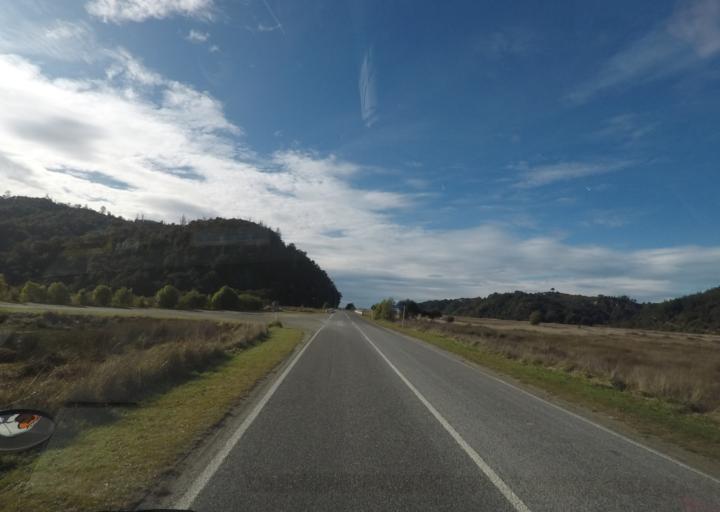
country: NZ
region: Tasman
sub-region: Tasman District
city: Motueka
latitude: -41.0153
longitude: 172.9910
